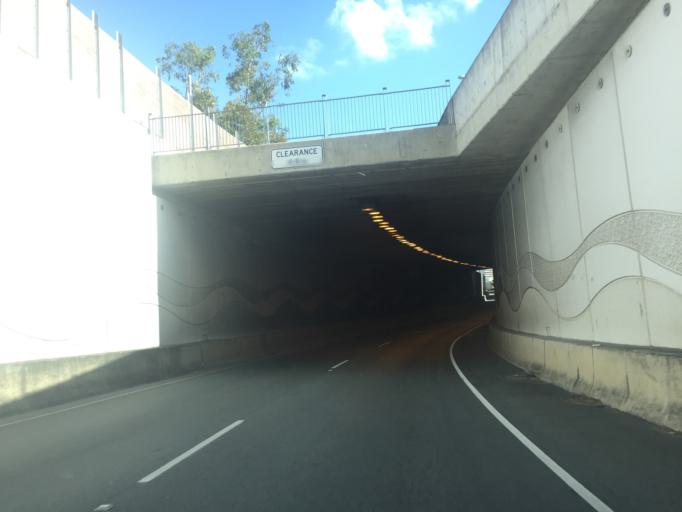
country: AU
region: Queensland
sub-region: Brisbane
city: Woolloongabba
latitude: -27.4939
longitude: 153.0344
